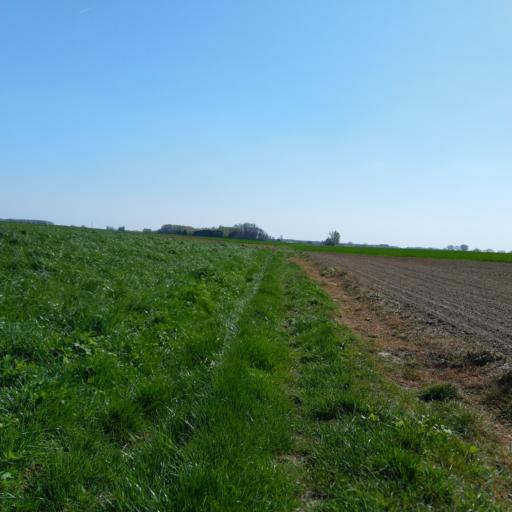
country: BE
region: Wallonia
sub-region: Province du Hainaut
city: Jurbise
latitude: 50.5543
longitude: 3.9370
